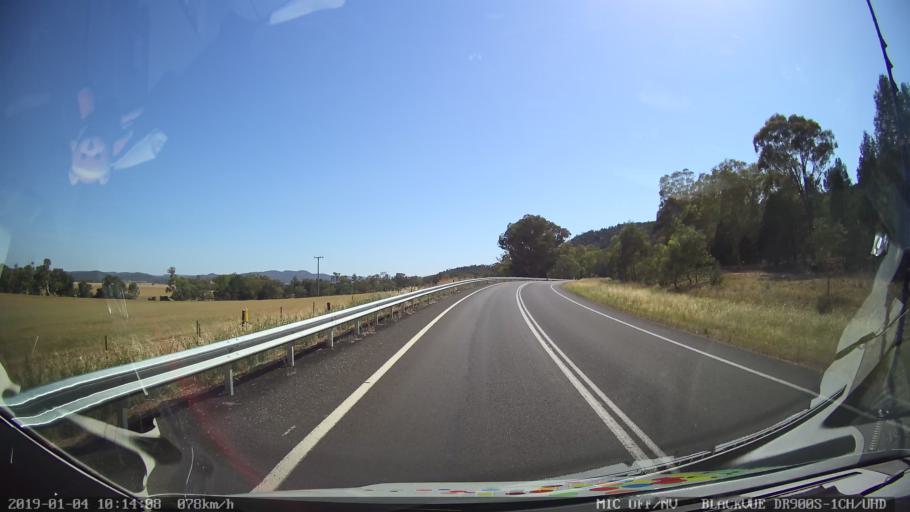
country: AU
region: New South Wales
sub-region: Cabonne
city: Canowindra
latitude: -33.3989
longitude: 148.4101
